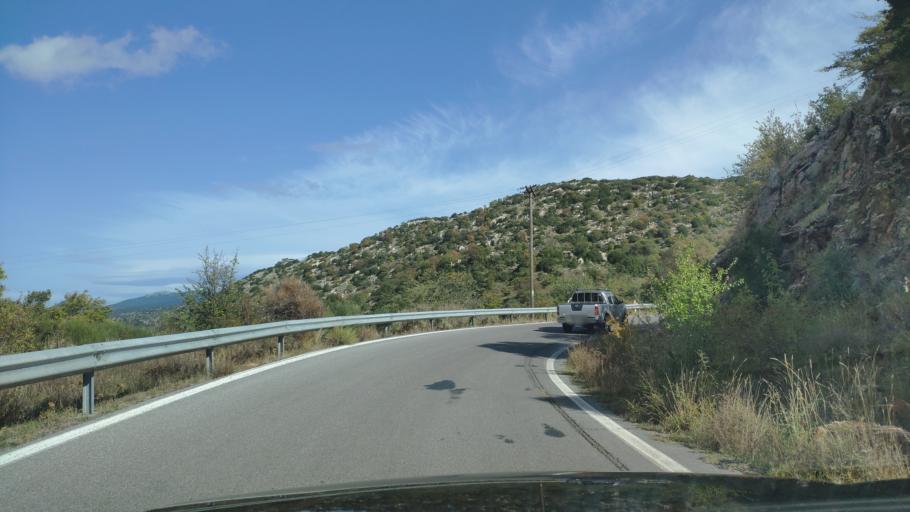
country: GR
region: Peloponnese
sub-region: Nomos Arkadias
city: Dimitsana
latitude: 37.5791
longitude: 22.0176
